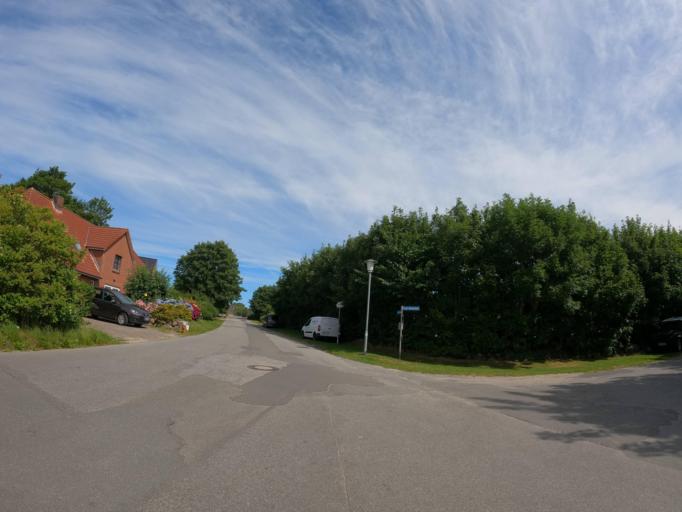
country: DE
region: Schleswig-Holstein
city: Sylt-Ost
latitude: 54.8704
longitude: 8.4444
